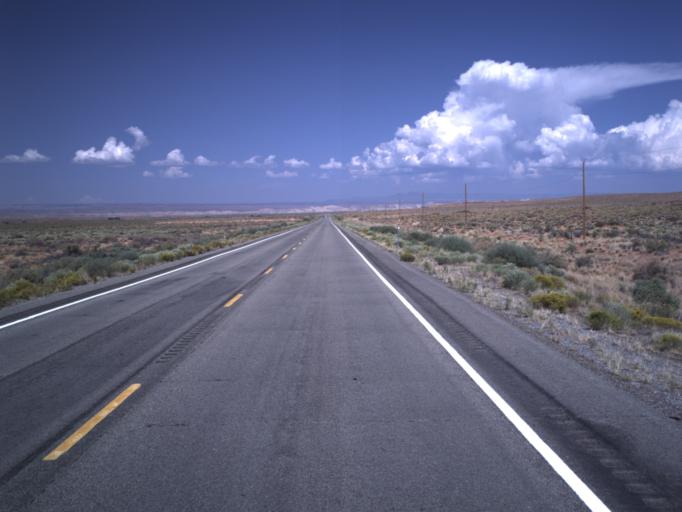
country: US
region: Utah
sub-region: San Juan County
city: Blanding
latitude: 37.1264
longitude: -109.5475
